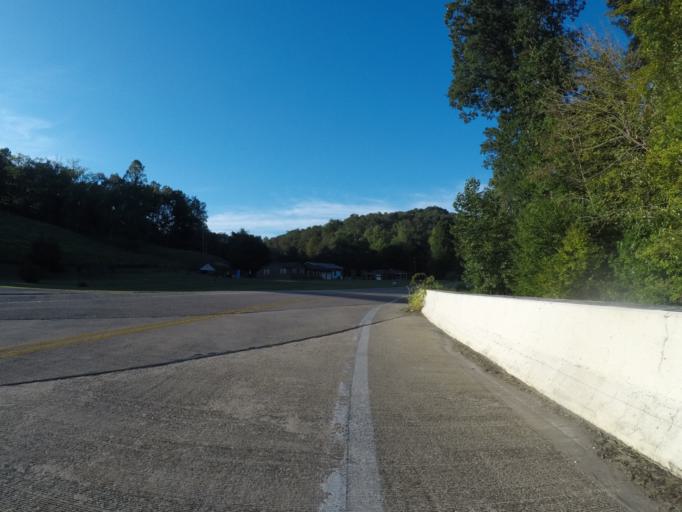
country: US
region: Ohio
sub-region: Lawrence County
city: Coal Grove
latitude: 38.5694
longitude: -82.5523
